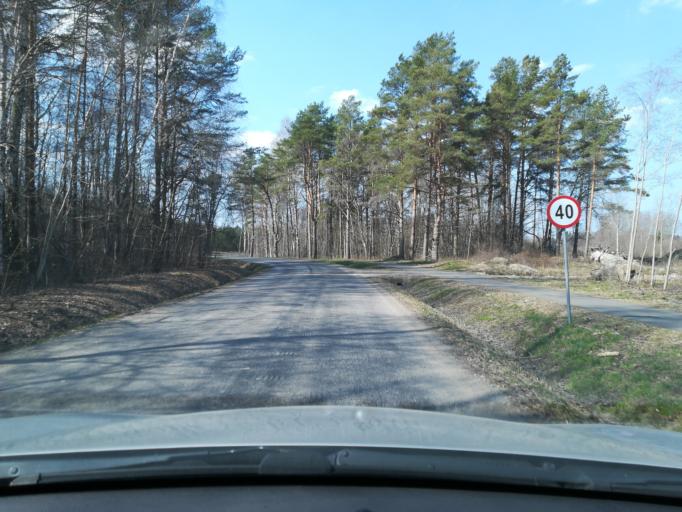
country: EE
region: Harju
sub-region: Saue vald
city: Laagri
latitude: 59.3548
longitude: 24.5818
